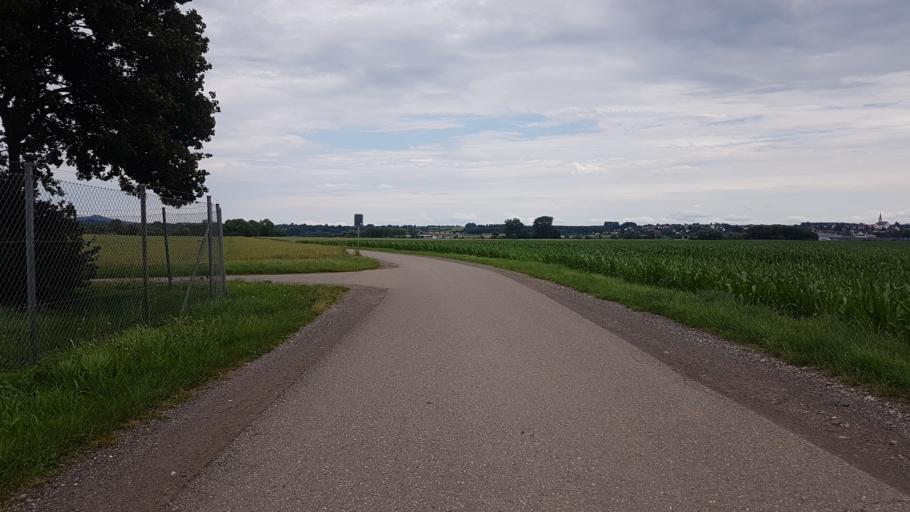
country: DE
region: Baden-Wuerttemberg
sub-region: Tuebingen Region
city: Ertingen
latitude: 48.1089
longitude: 9.4396
